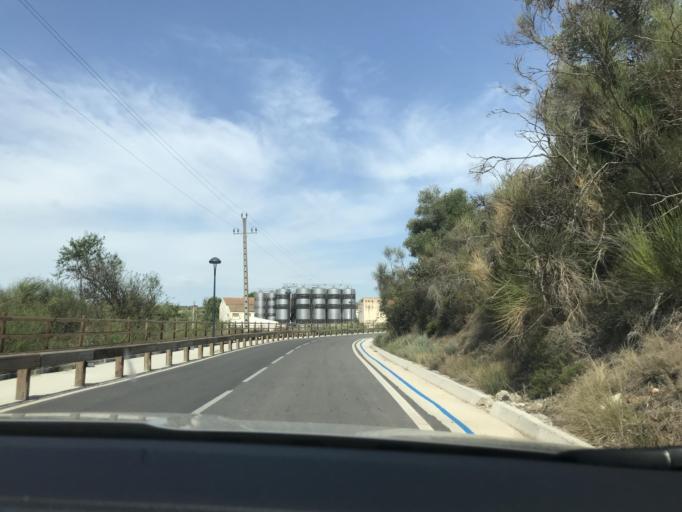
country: ES
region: Catalonia
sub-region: Provincia de Tarragona
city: Salomo
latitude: 41.2249
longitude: 1.3762
